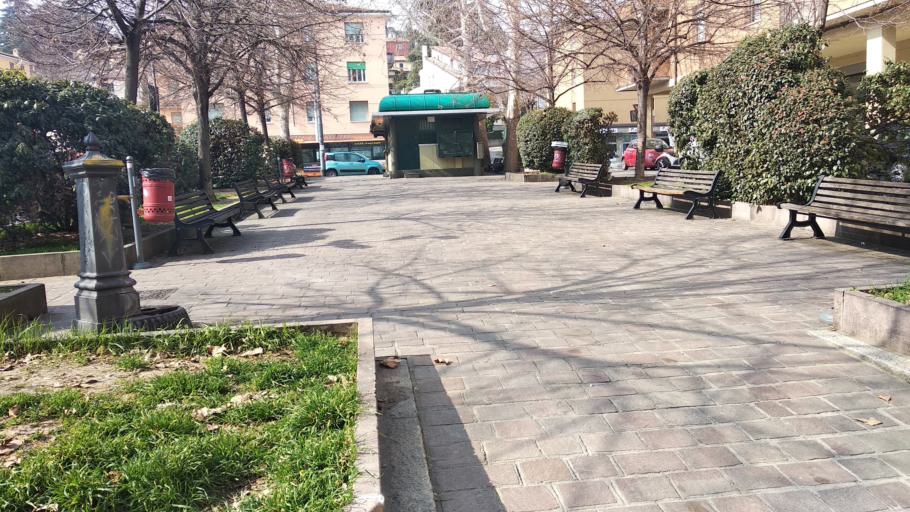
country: IT
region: Emilia-Romagna
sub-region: Provincia di Bologna
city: Ponticella
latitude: 44.4569
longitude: 11.3701
